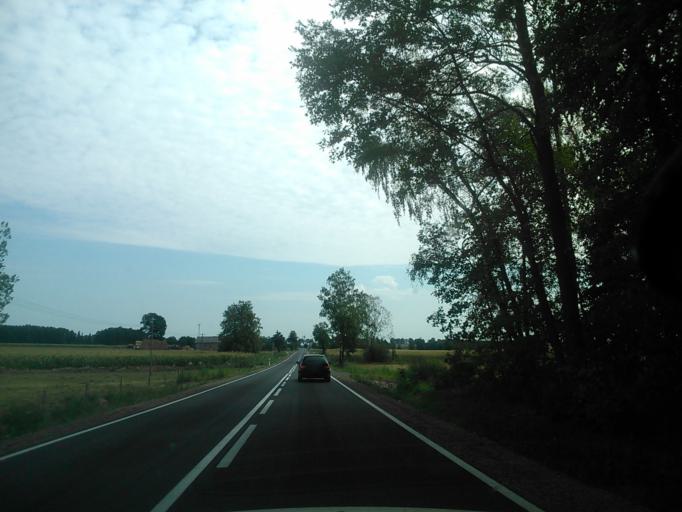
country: PL
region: Warmian-Masurian Voivodeship
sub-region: Powiat dzialdowski
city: Lidzbark
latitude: 53.2305
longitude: 19.9790
